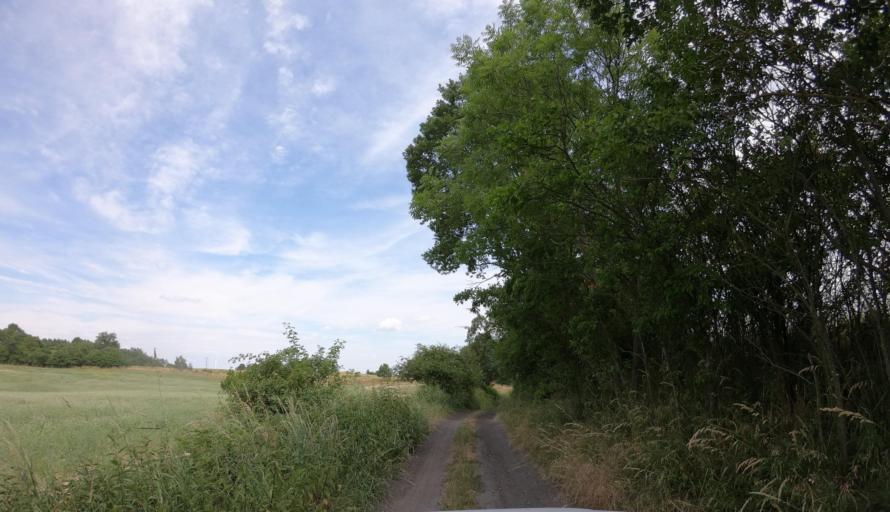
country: PL
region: West Pomeranian Voivodeship
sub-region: Powiat pyrzycki
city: Kozielice
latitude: 53.0309
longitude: 14.7559
